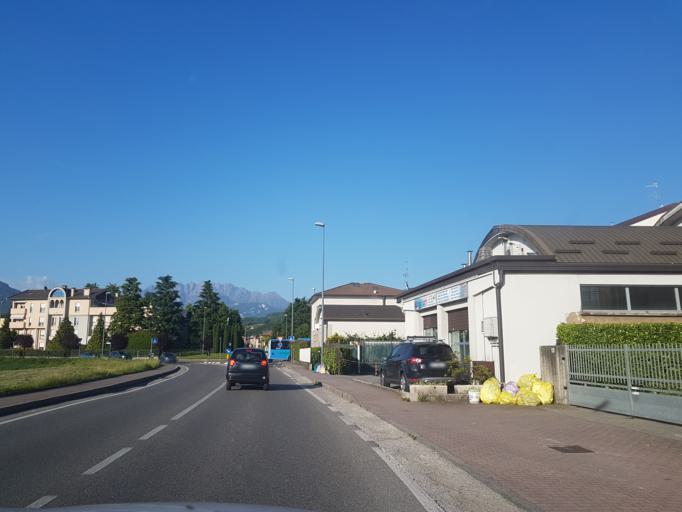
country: IT
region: Lombardy
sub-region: Provincia di Lecco
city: Oggiono
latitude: 45.7872
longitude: 9.3395
